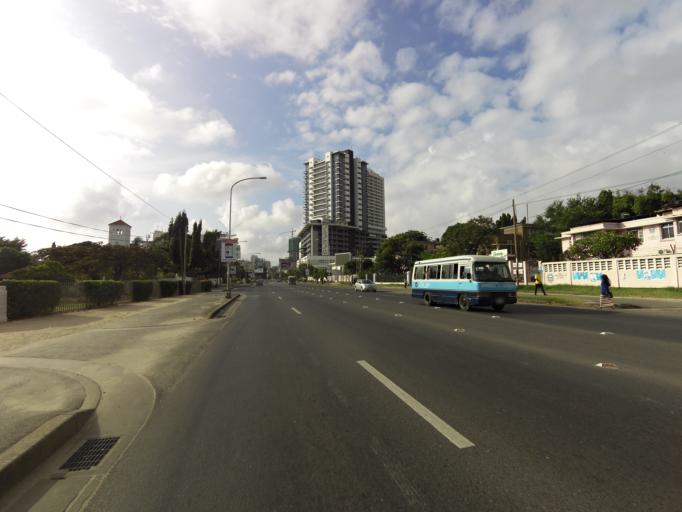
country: TZ
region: Dar es Salaam
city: Dar es Salaam
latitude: -6.8074
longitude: 39.2866
